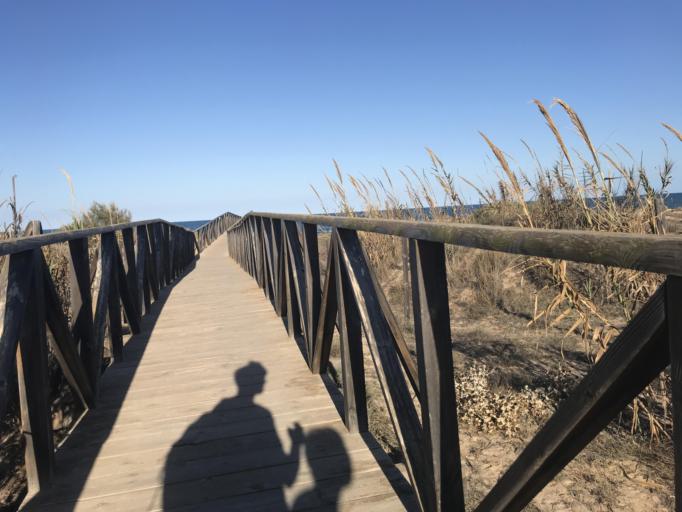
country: ES
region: Valencia
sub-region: Provincia de Alicante
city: Guardamar del Segura
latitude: 38.0322
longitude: -0.6522
